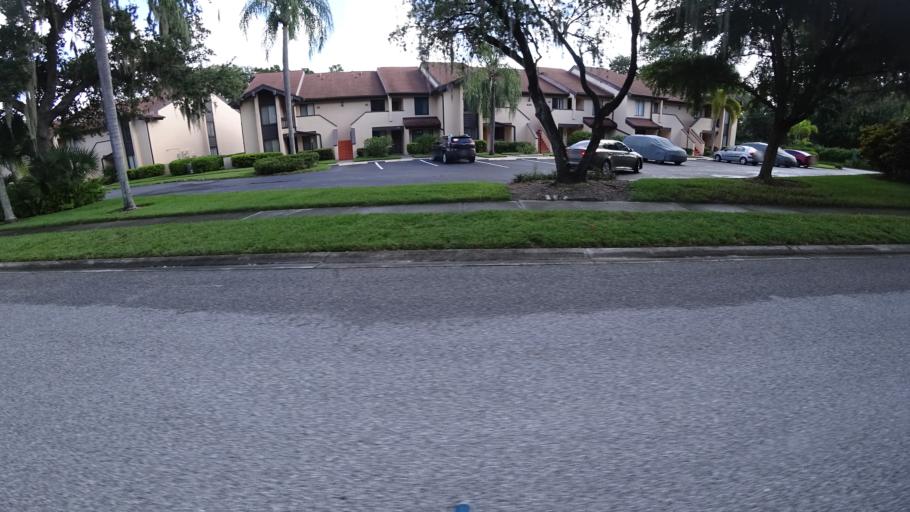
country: US
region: Florida
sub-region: Sarasota County
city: Desoto Lakes
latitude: 27.3931
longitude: -82.4814
